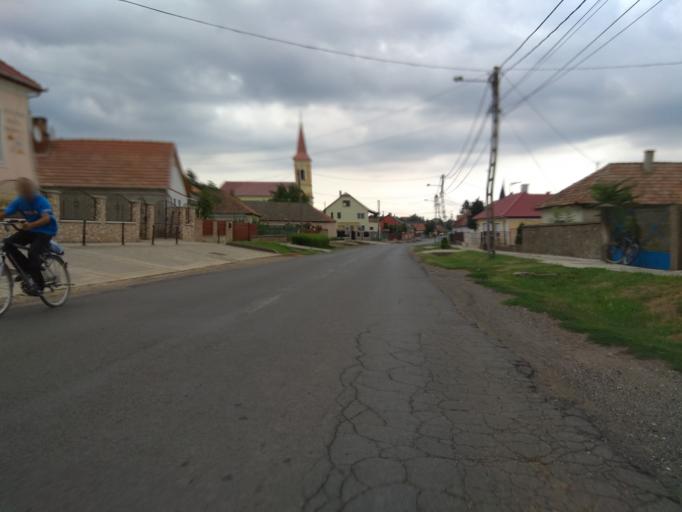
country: HU
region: Borsod-Abauj-Zemplen
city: Bekecs
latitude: 48.1597
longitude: 21.1517
